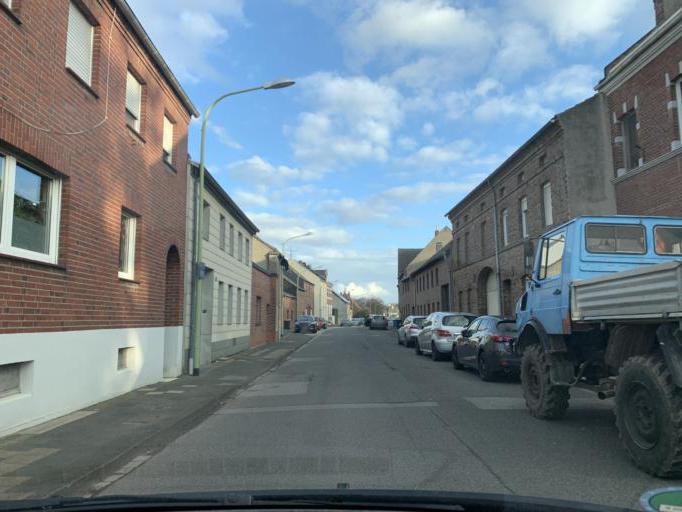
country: DE
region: North Rhine-Westphalia
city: Julich
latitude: 50.9224
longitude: 6.4052
